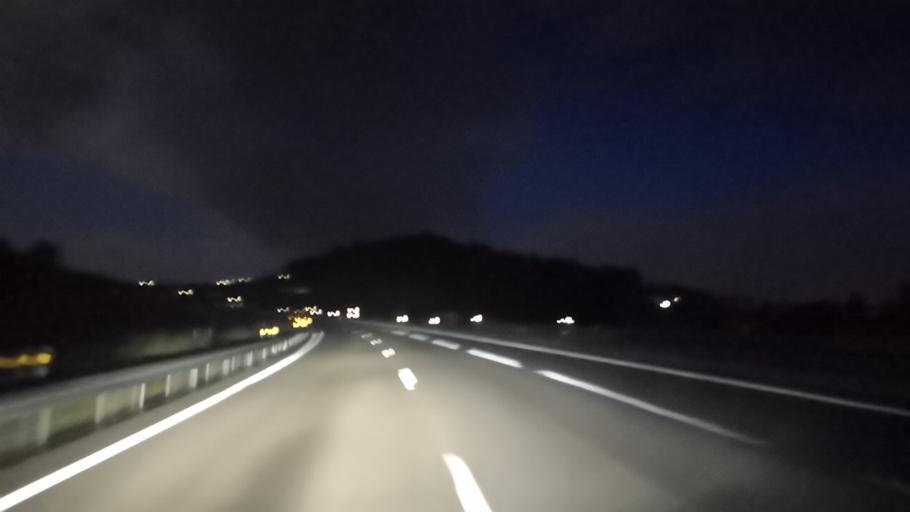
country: PT
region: Porto
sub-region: Lousada
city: Meinedo
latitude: 41.2802
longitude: -8.2453
